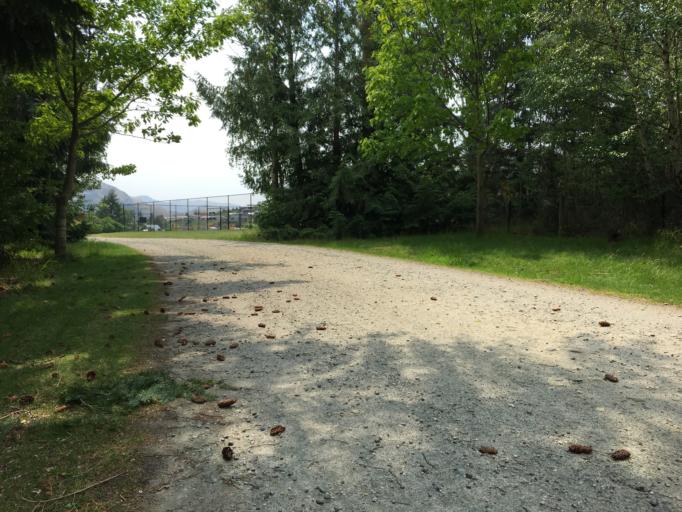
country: NZ
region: Otago
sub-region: Queenstown-Lakes District
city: Queenstown
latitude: -45.0462
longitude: 168.6912
